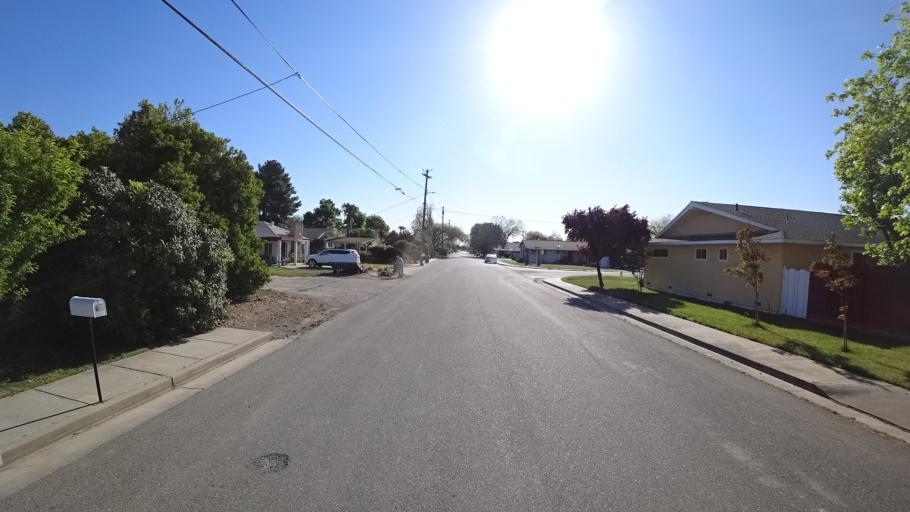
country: US
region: California
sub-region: Glenn County
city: Orland
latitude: 39.7416
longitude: -122.1893
